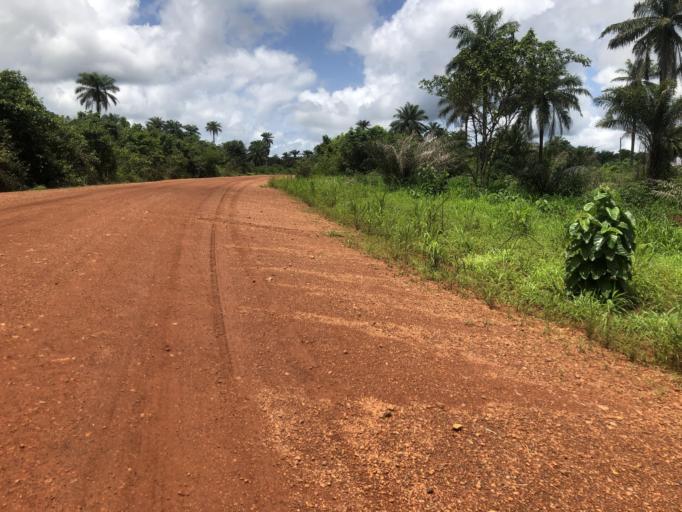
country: SL
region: Northern Province
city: Port Loko
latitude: 8.7177
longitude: -12.8367
